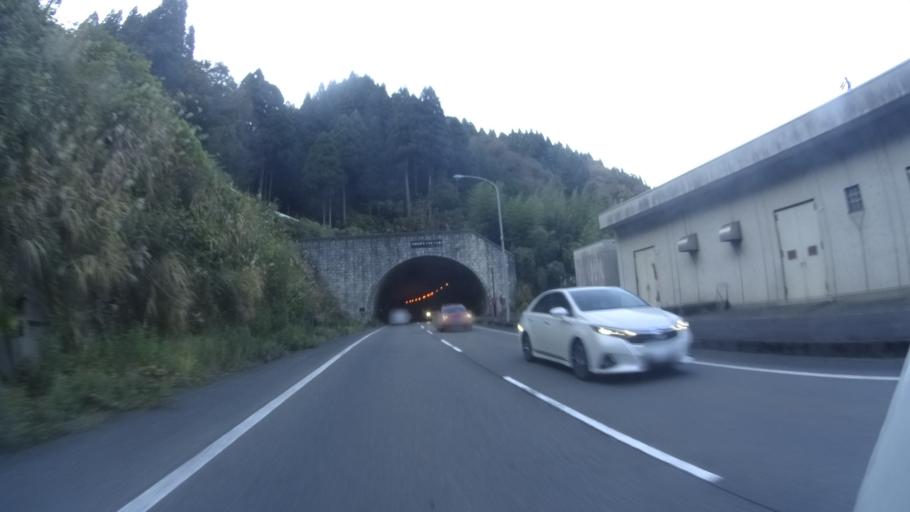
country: JP
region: Fukui
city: Ono
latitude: 36.0078
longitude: 136.3508
